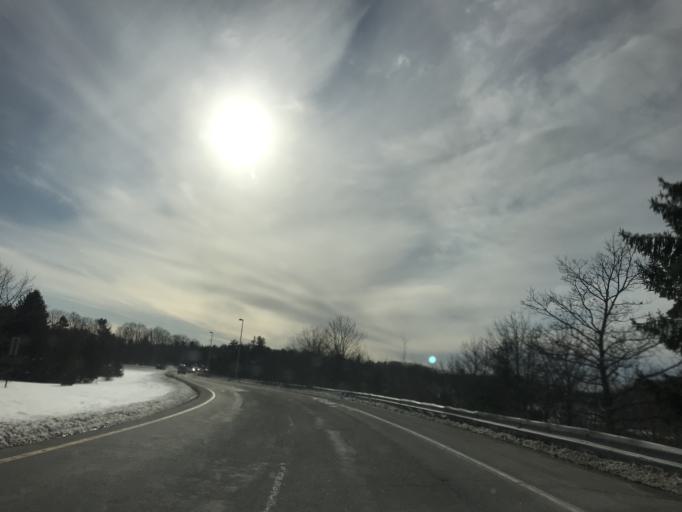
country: US
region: Maine
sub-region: Cumberland County
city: South Portland Gardens
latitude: 43.6393
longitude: -70.2960
